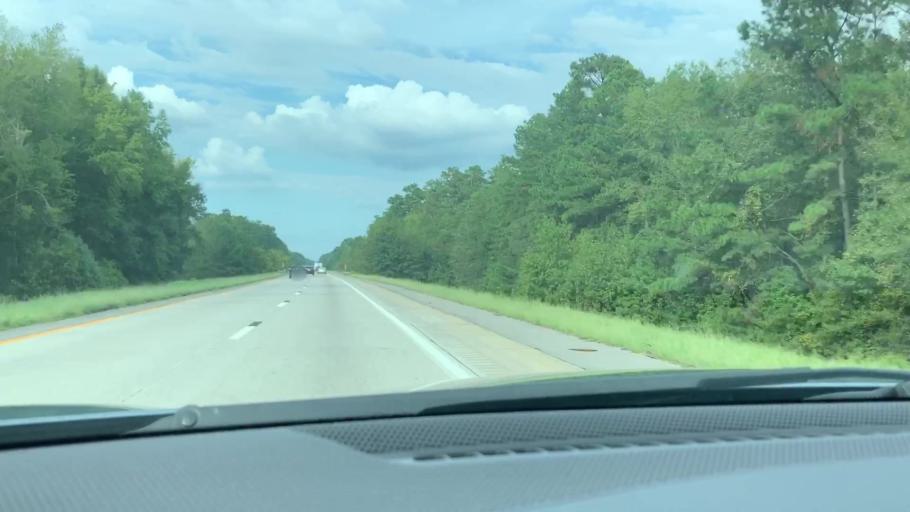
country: US
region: South Carolina
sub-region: Dorchester County
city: Saint George
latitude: 33.1011
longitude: -80.6450
